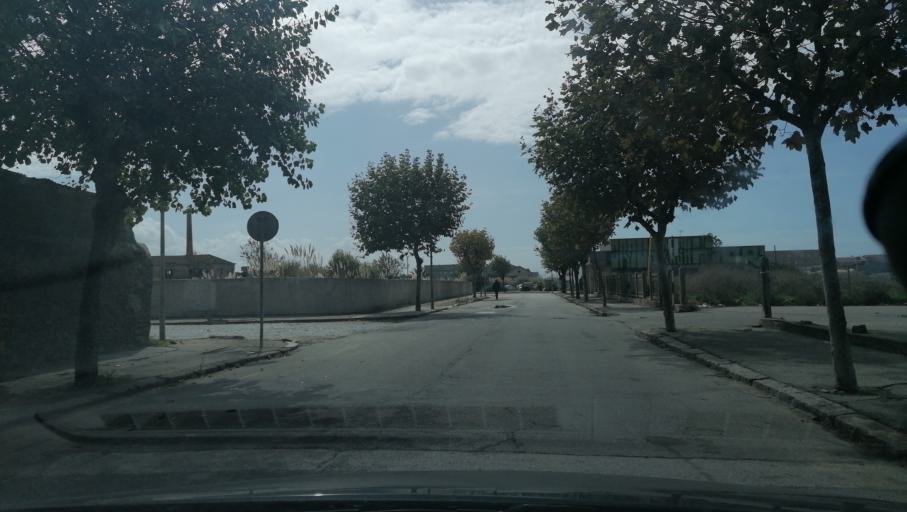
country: PT
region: Aveiro
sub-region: Espinho
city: Espinho
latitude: 41.0013
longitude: -8.6424
